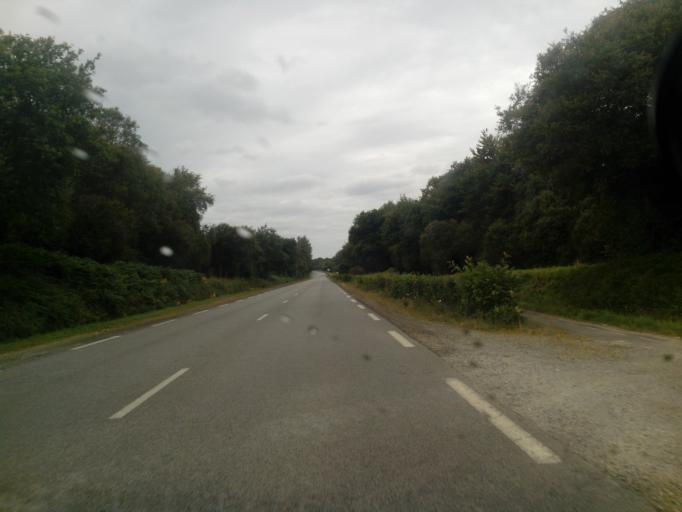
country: FR
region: Brittany
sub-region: Departement du Morbihan
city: Kervignac
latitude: 47.7600
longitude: -3.2563
